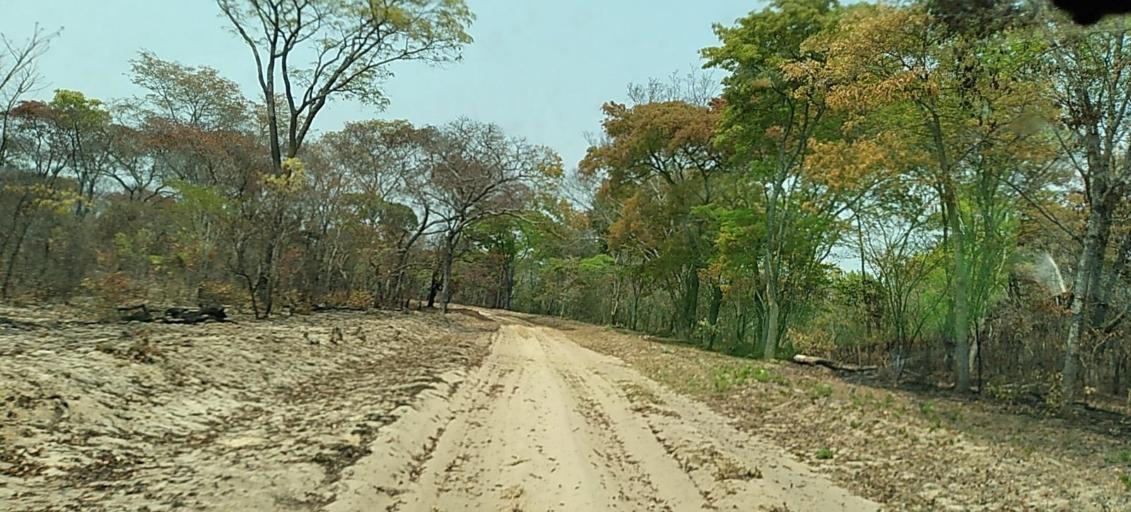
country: ZM
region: North-Western
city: Zambezi
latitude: -13.9363
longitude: 23.2226
